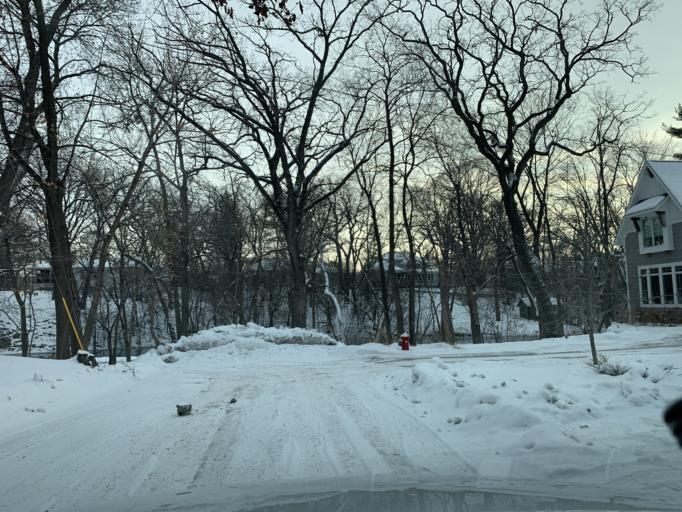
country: US
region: Minnesota
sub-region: Hennepin County
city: Saint Louis Park
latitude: 44.9210
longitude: -93.3516
